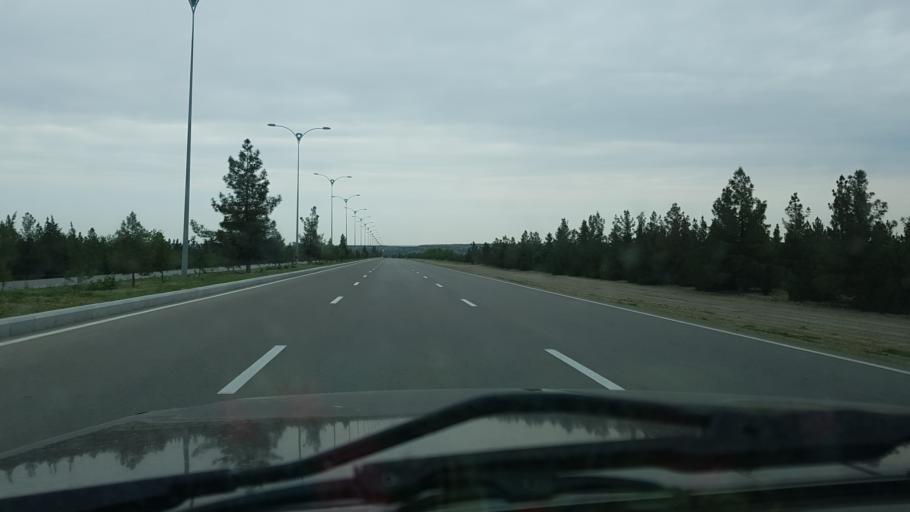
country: TM
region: Ahal
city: Ashgabat
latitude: 37.9165
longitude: 58.2485
